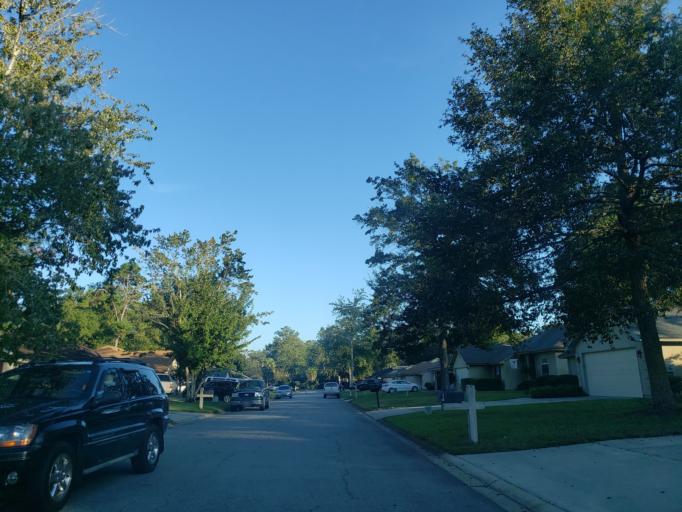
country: US
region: Georgia
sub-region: Chatham County
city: Isle of Hope
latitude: 31.9903
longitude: -81.0719
